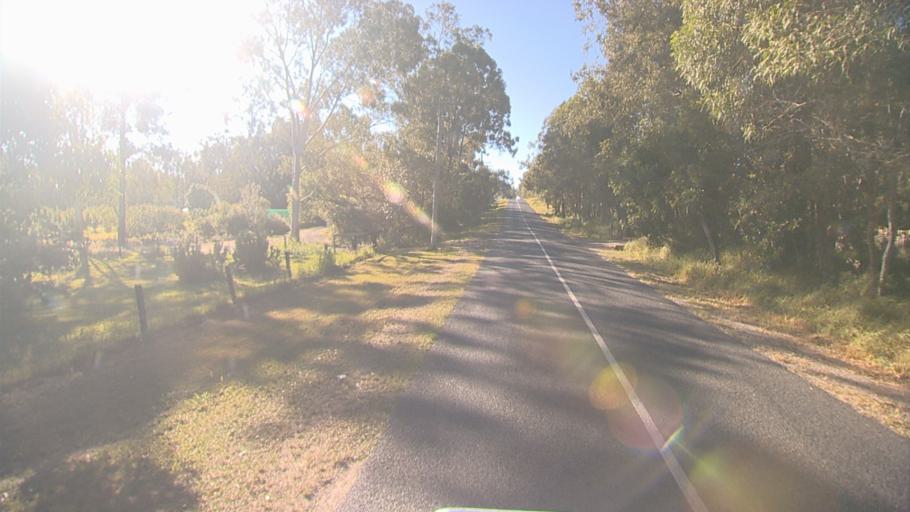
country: AU
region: Queensland
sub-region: Logan
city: Logan Reserve
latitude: -27.7332
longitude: 153.1040
